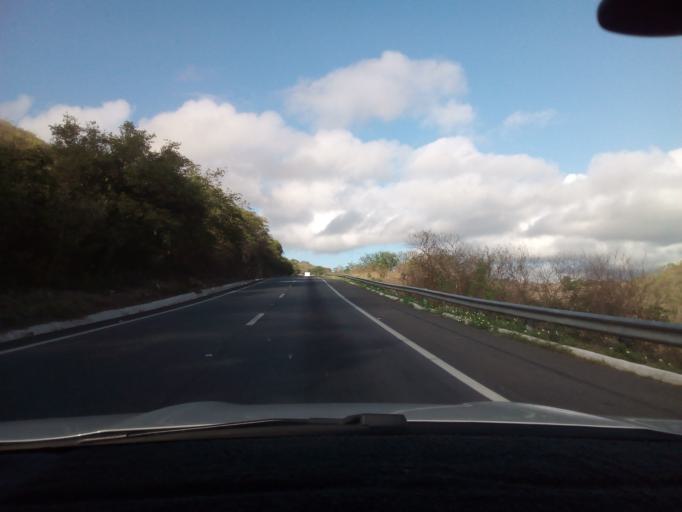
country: BR
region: Paraiba
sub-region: Inga
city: Inga
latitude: -7.2478
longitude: -35.6795
